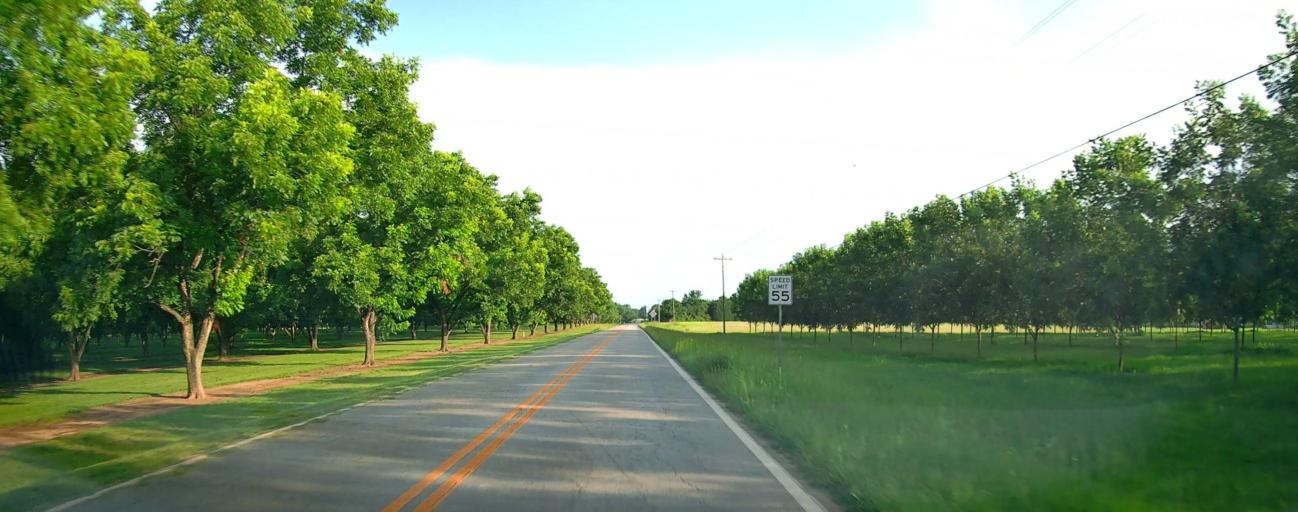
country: US
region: Georgia
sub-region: Peach County
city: Byron
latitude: 32.6734
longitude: -83.8609
